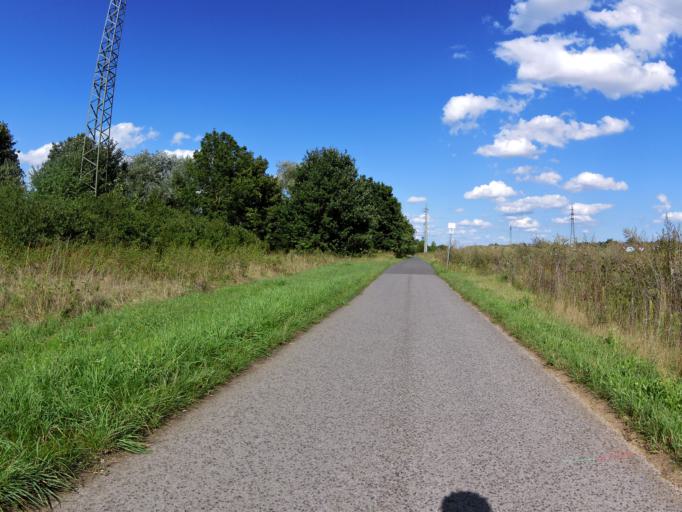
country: DE
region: Bavaria
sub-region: Regierungsbezirk Unterfranken
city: Sulzfeld am Main
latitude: 49.7124
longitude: 10.1422
